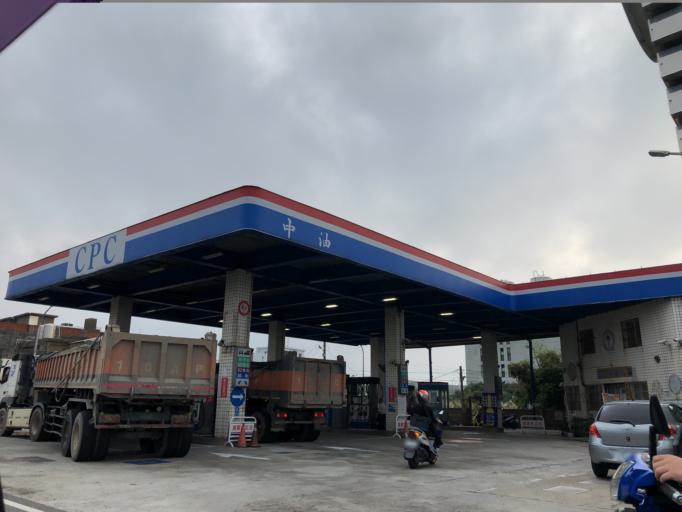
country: TW
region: Taiwan
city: Taoyuan City
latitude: 25.1039
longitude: 121.2473
